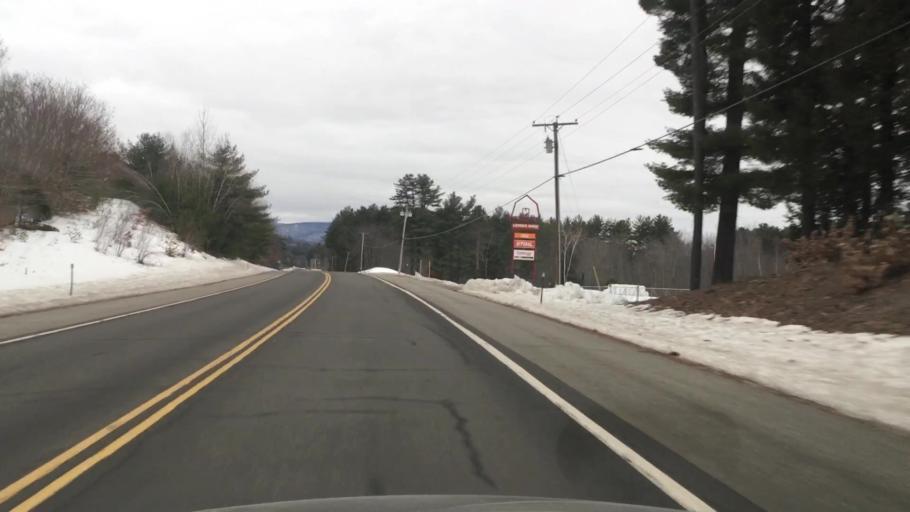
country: US
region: New Hampshire
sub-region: Merrimack County
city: Sutton
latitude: 43.2559
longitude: -71.9328
